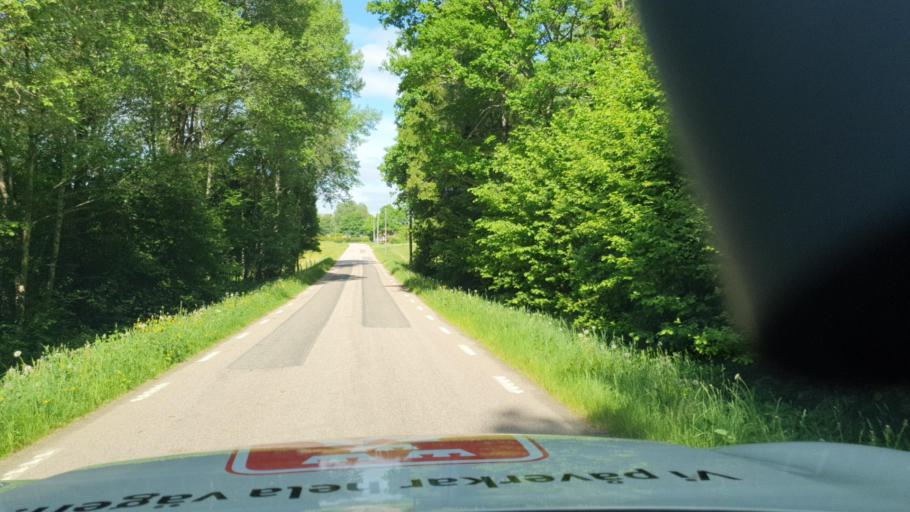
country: SE
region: Vaestra Goetaland
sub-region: Herrljunga Kommun
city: Herrljunga
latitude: 57.9302
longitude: 13.0608
